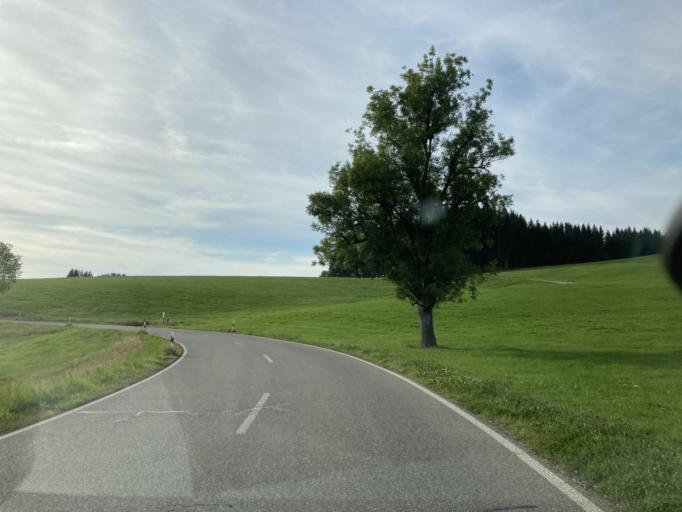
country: DE
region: Baden-Wuerttemberg
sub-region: Freiburg Region
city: Gutenbach
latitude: 47.9834
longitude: 8.1619
